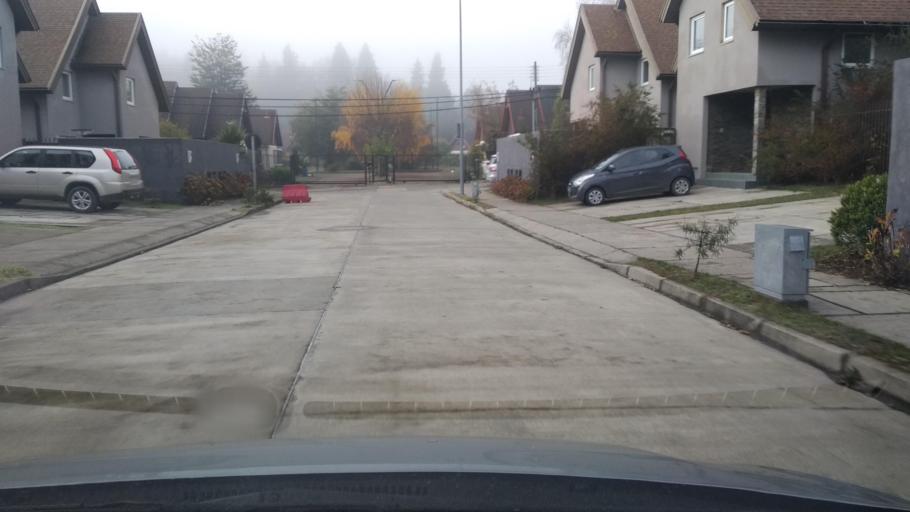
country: CL
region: Los Rios
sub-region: Provincia de Valdivia
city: Valdivia
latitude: -39.8105
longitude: -73.2601
